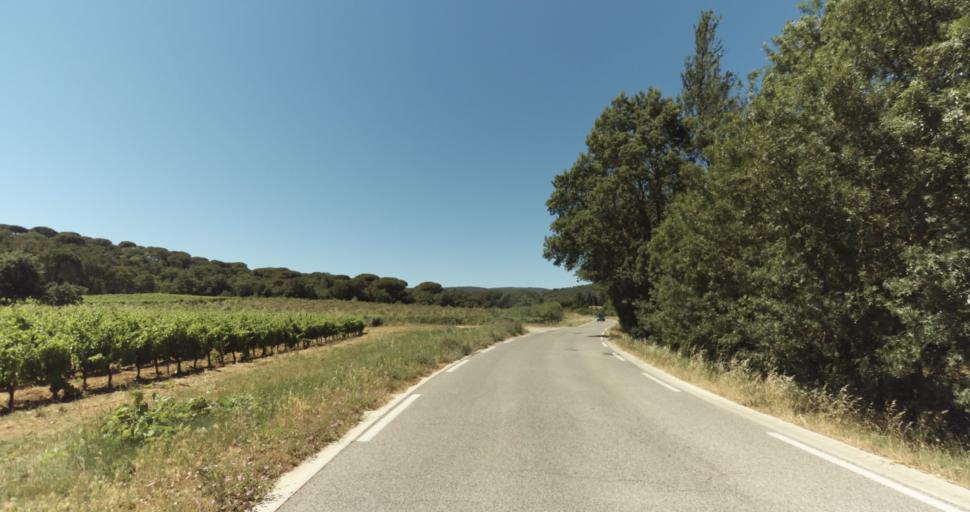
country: FR
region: Provence-Alpes-Cote d'Azur
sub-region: Departement du Var
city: Gassin
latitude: 43.2460
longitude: 6.5774
